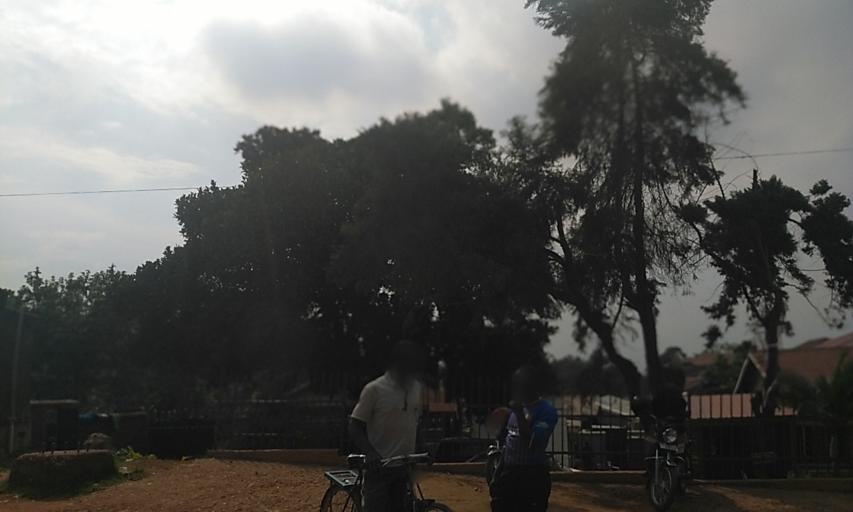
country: UG
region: Central Region
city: Kampala Central Division
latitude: 0.3058
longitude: 32.5611
